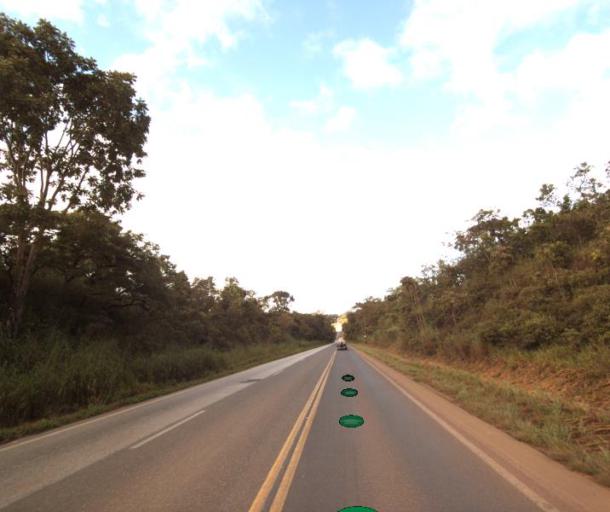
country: BR
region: Goias
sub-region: Uruacu
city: Uruacu
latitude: -14.5861
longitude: -49.1611
